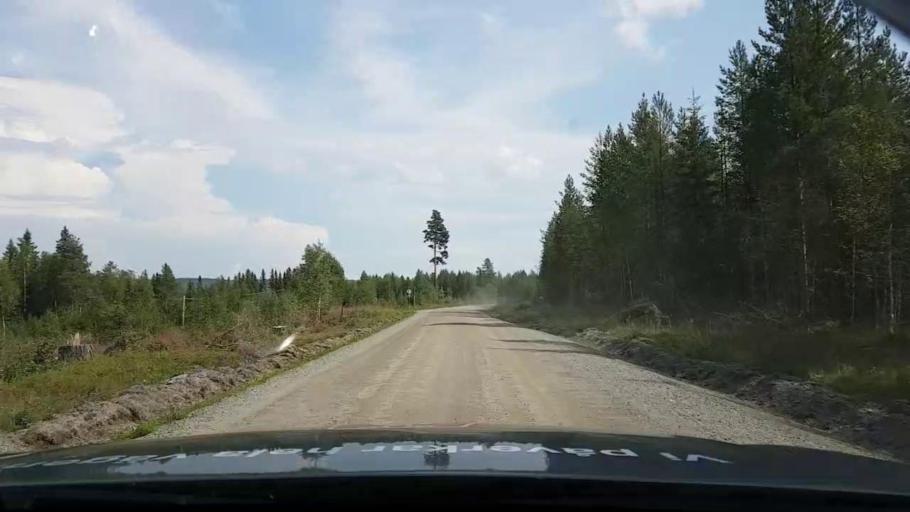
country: SE
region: Jaemtland
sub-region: Braecke Kommun
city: Braecke
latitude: 62.7347
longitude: 15.4672
